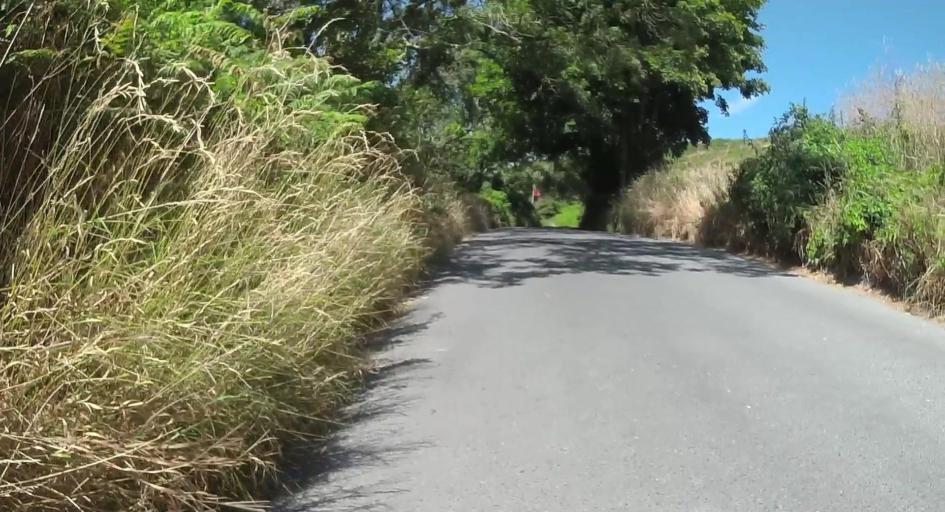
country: GB
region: England
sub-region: Dorset
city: Wareham
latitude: 50.6325
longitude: -2.1344
